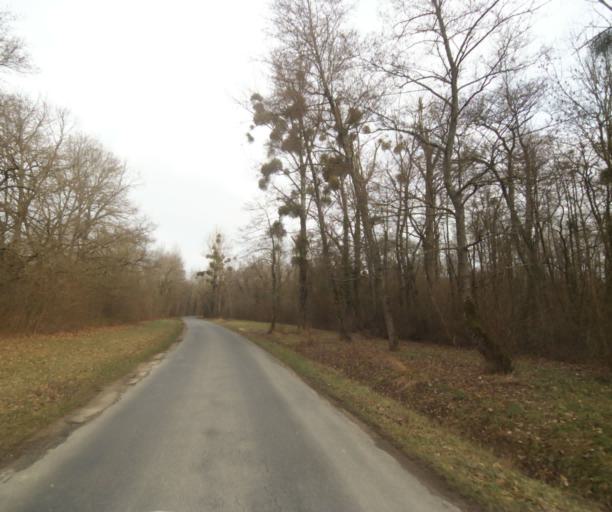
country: FR
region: Champagne-Ardenne
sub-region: Departement de la Haute-Marne
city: Villiers-en-Lieu
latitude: 48.6656
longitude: 4.8336
